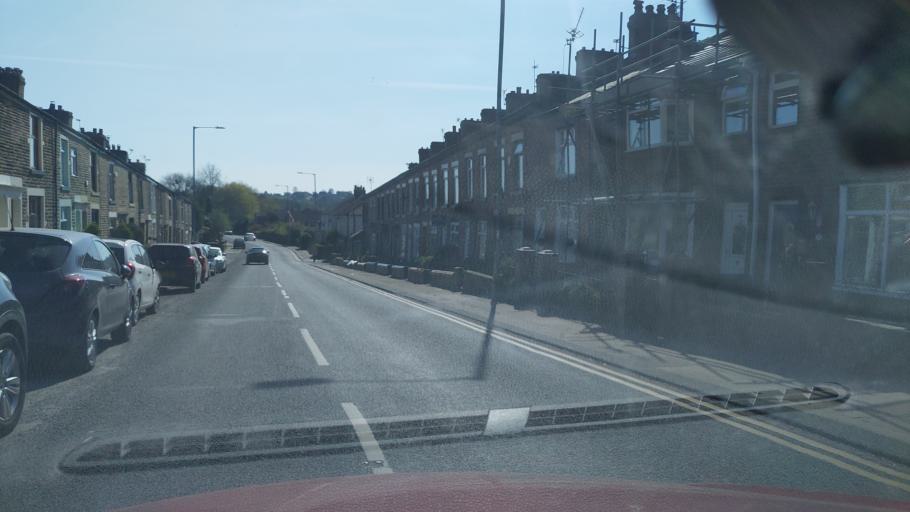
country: GB
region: England
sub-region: Borough of Bolton
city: Horwich
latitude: 53.5973
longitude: -2.5599
